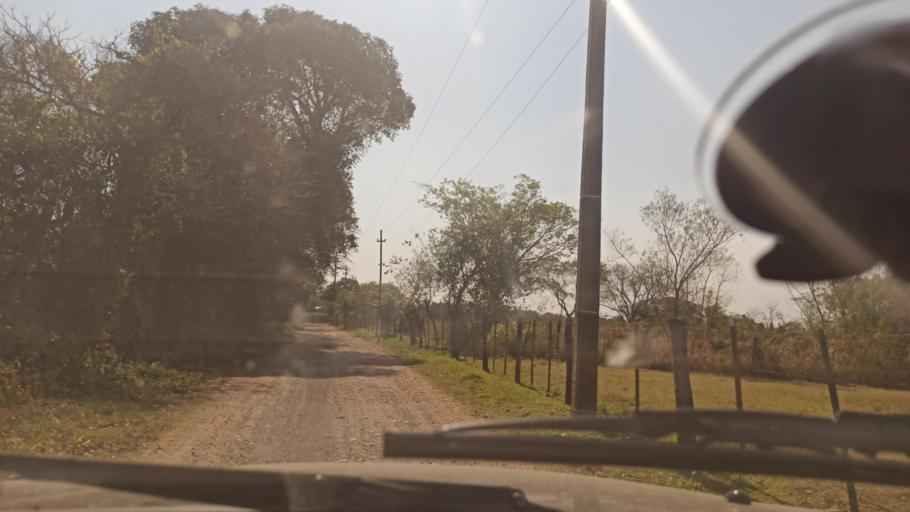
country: AR
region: Formosa
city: Clorinda
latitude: -25.3251
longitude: -57.6918
